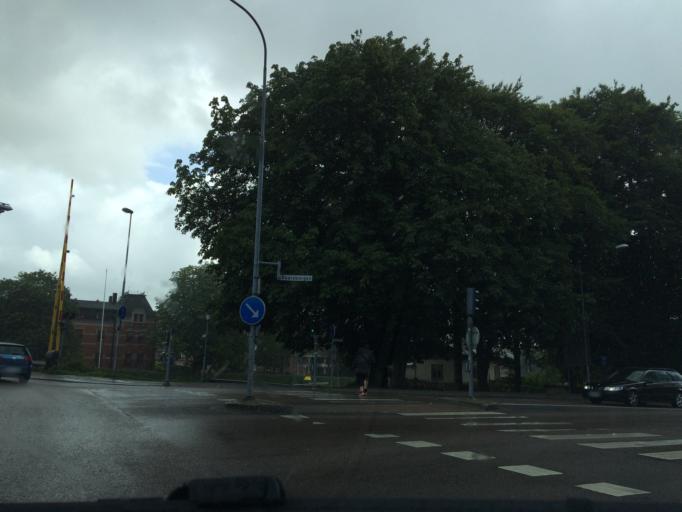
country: SE
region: Vaestra Goetaland
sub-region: Trollhattan
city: Trollhattan
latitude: 58.2842
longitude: 12.2830
